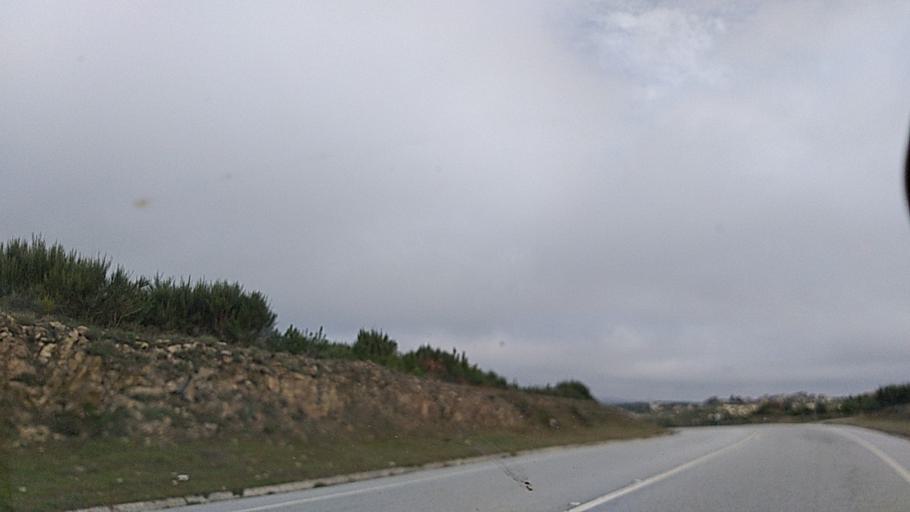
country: PT
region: Guarda
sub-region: Aguiar da Beira
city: Aguiar da Beira
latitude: 40.7620
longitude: -7.5021
